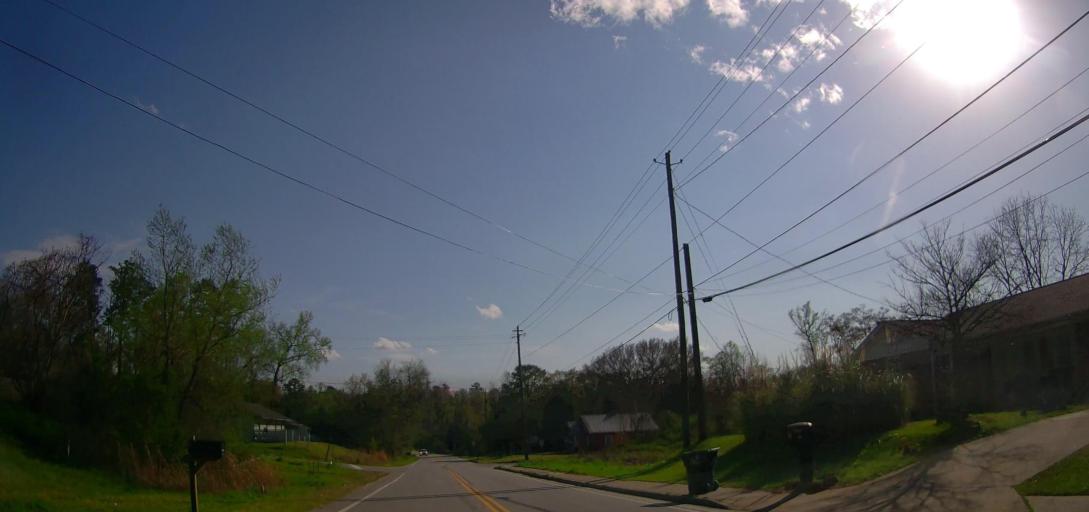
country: US
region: Georgia
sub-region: Baldwin County
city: Hardwick
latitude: 33.0505
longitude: -83.2310
